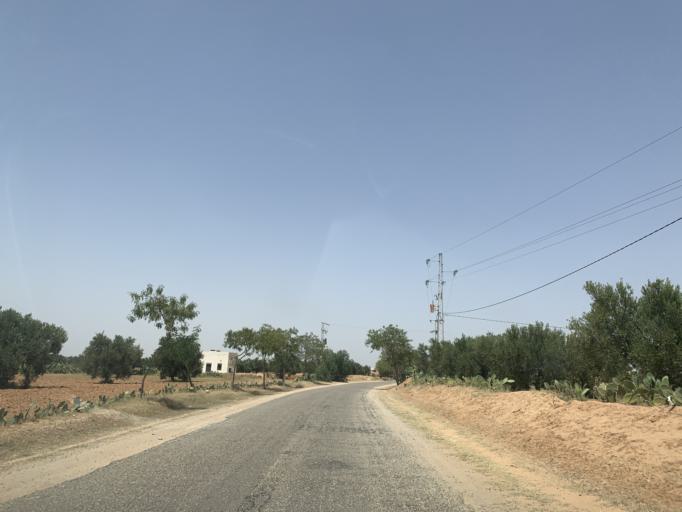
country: TN
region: Al Mahdiyah
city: Shurban
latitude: 35.1874
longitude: 10.2437
